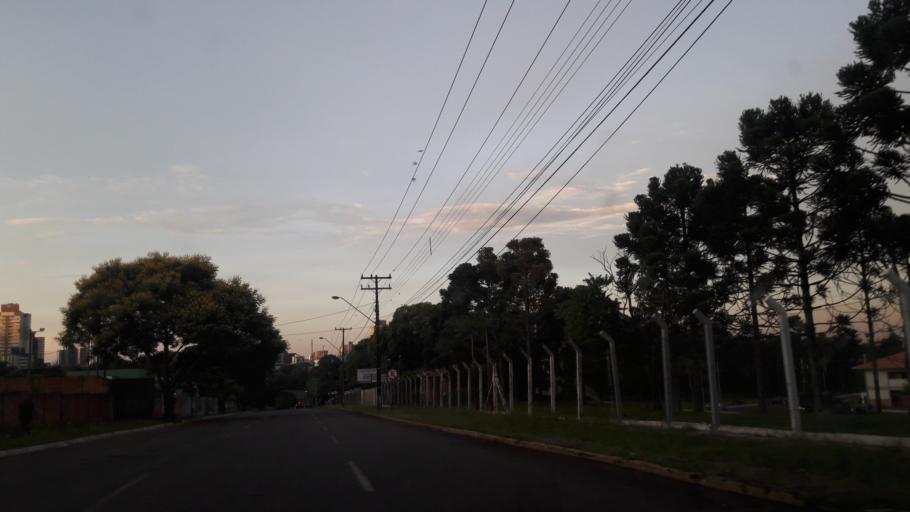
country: BR
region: Parana
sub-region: Cascavel
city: Cascavel
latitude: -24.9620
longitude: -53.4501
